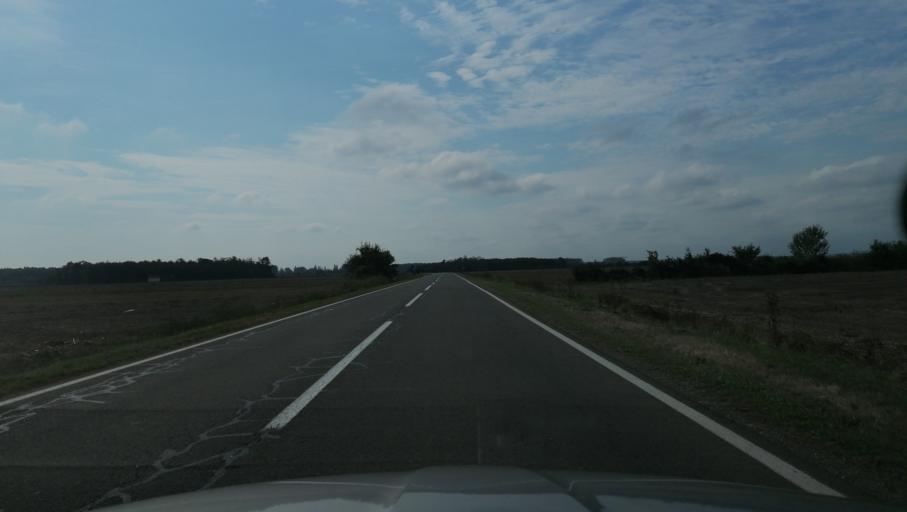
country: RS
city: Bosut
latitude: 44.9598
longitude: 19.3814
